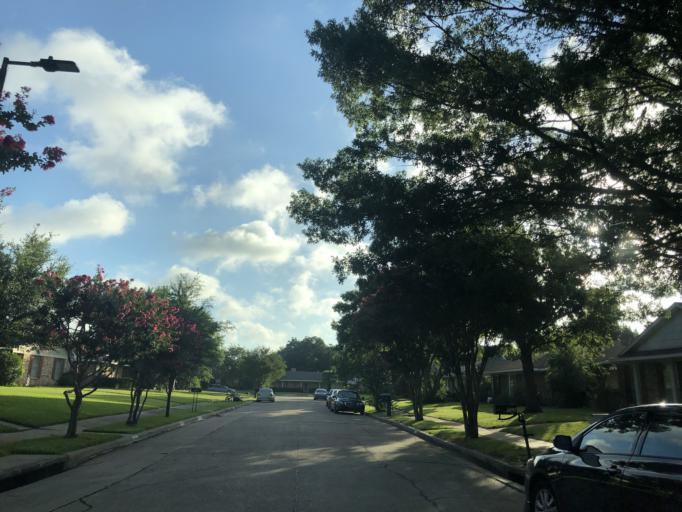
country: US
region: Texas
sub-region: Dallas County
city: Garland
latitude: 32.8493
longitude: -96.6307
